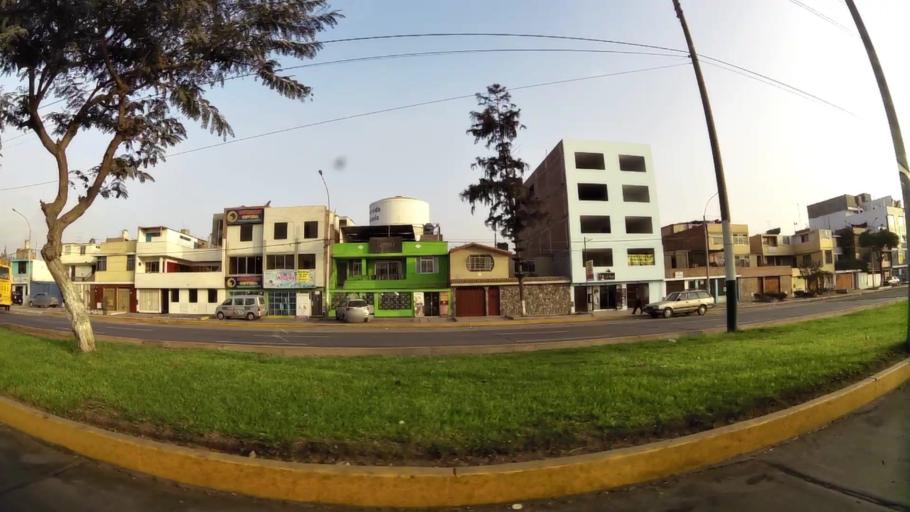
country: PE
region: Lima
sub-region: Lima
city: Independencia
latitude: -11.9917
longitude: -77.0758
